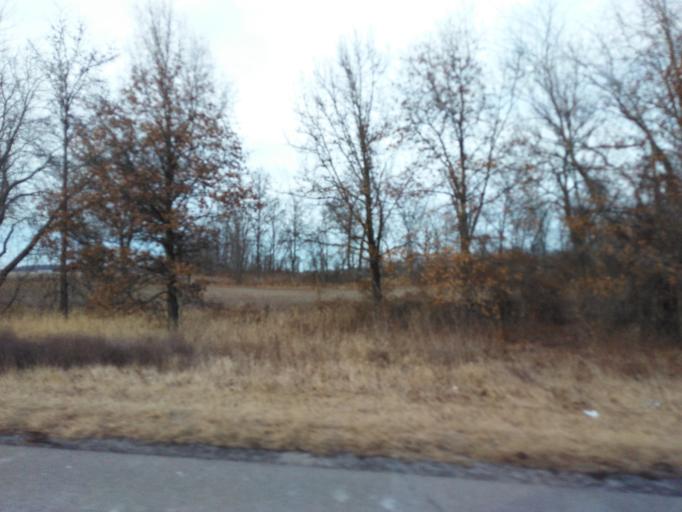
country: US
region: Illinois
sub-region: Jefferson County
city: Mount Vernon
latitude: 38.3473
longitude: -88.9796
